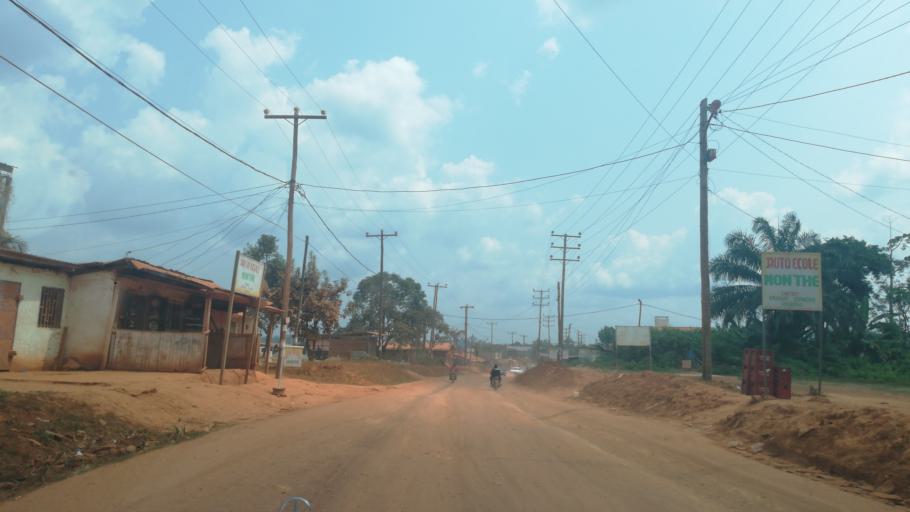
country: CM
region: Centre
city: Yaounde
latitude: 3.7857
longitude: 11.4913
